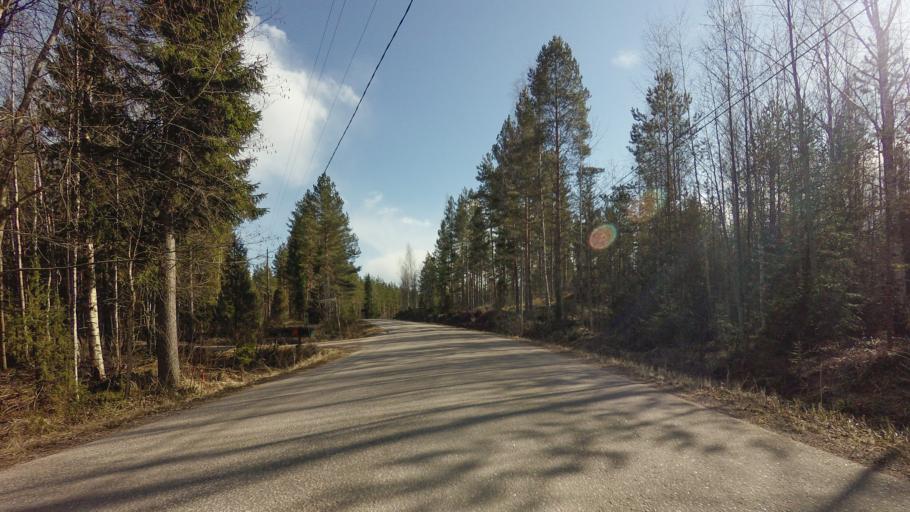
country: FI
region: Varsinais-Suomi
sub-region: Salo
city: Suomusjaervi
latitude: 60.3395
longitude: 23.6502
